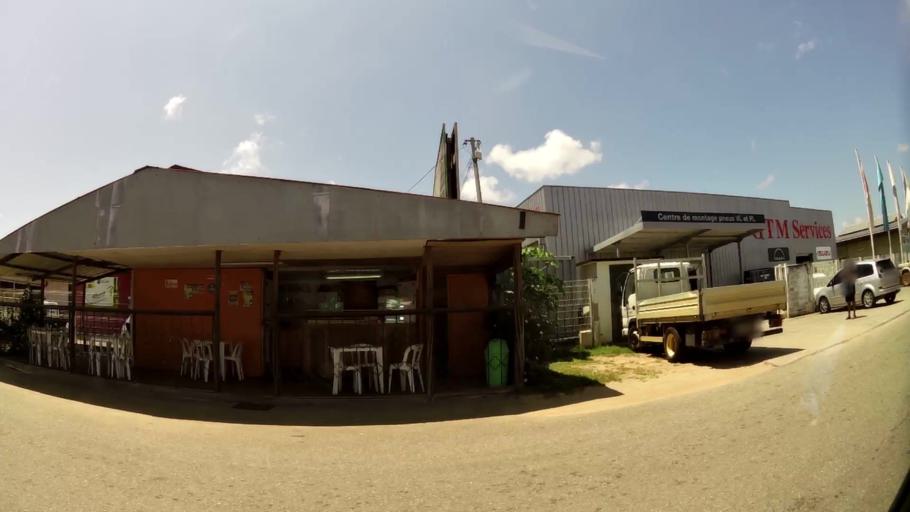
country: GF
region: Guyane
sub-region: Guyane
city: Cayenne
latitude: 4.9053
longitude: -52.3258
